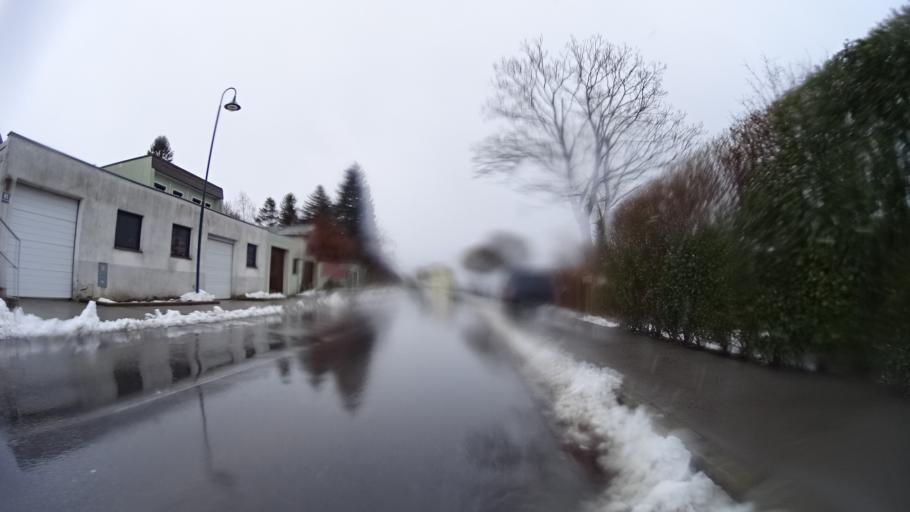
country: AT
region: Lower Austria
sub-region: Politischer Bezirk Korneuburg
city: Leobendorf
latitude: 48.3784
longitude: 16.2916
